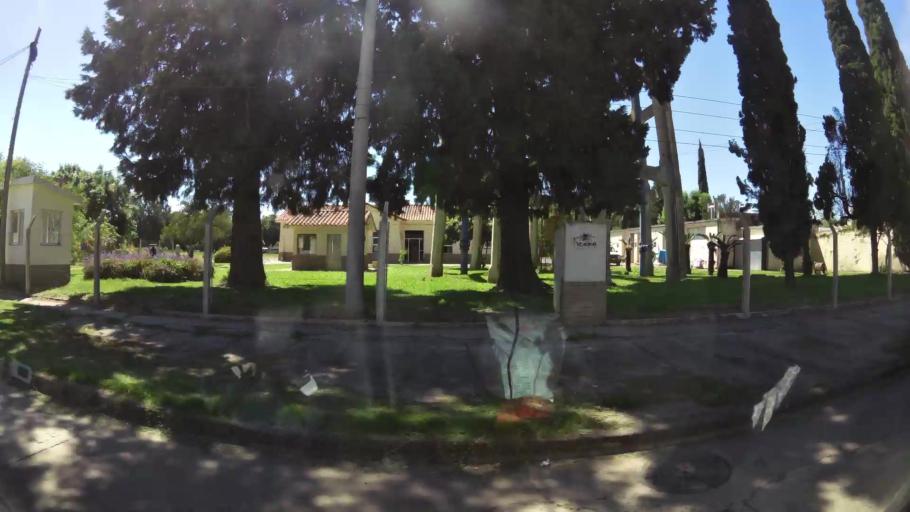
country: AR
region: Santa Fe
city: Esperanza
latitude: -31.4426
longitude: -60.9262
